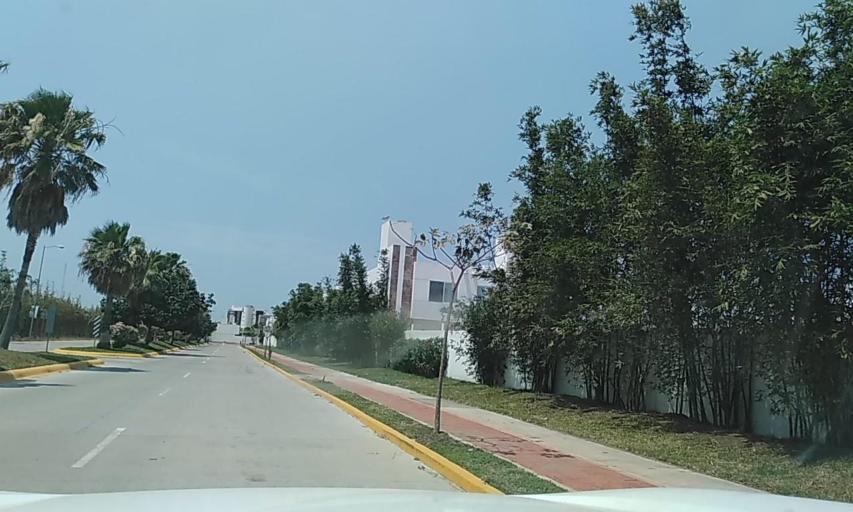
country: MX
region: Veracruz
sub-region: Veracruz
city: Hacienda Sotavento
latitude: 19.1271
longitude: -96.1722
